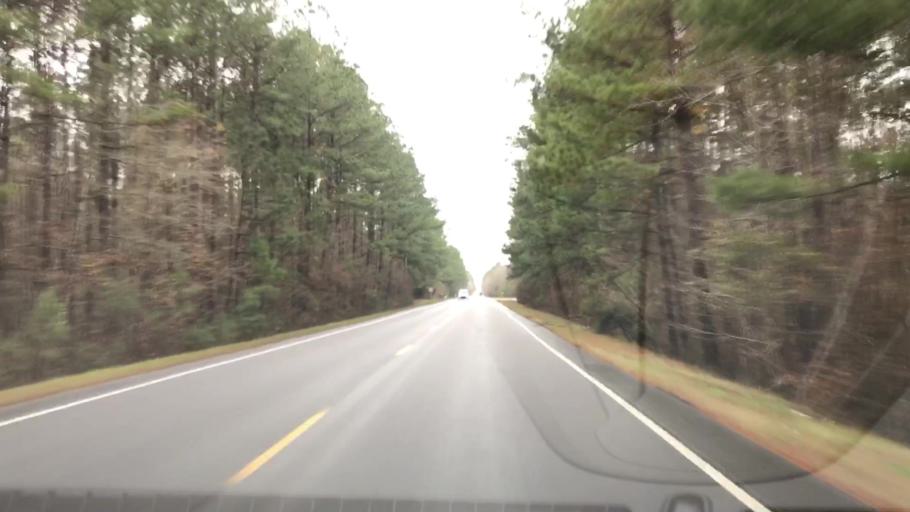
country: US
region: South Carolina
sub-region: Berkeley County
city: Saint Stephen
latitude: 33.2897
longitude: -79.8025
